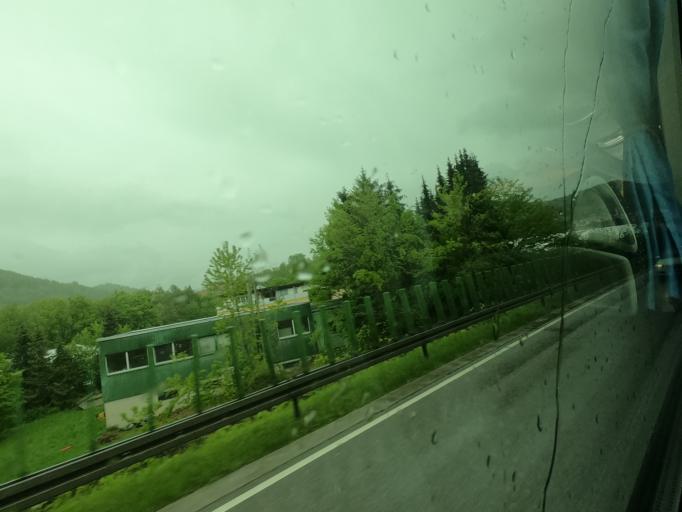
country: DE
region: Baden-Wuerttemberg
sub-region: Regierungsbezirk Stuttgart
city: Oberkochen
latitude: 48.8148
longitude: 10.1242
